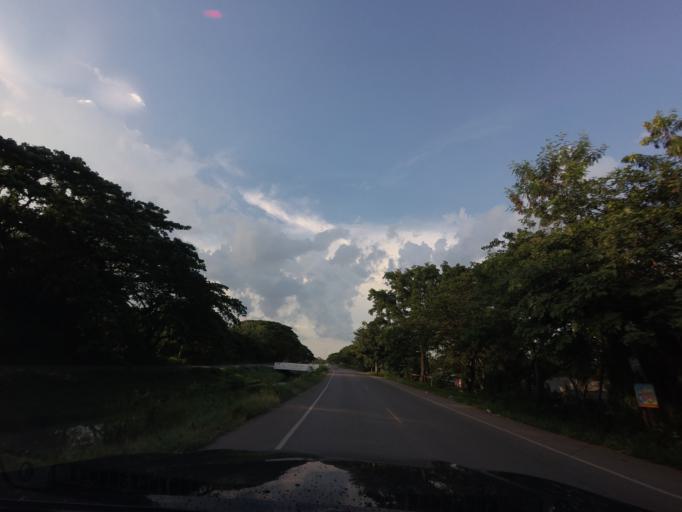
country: TH
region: Khon Kaen
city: Khon Kaen
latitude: 16.4138
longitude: 102.8624
